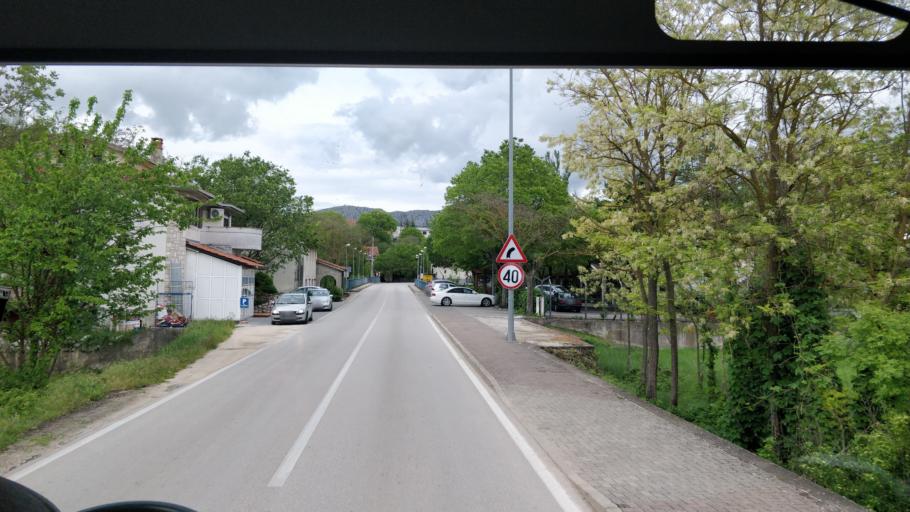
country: BA
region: Federation of Bosnia and Herzegovina
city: Ljubuski
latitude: 43.1827
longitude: 17.5220
